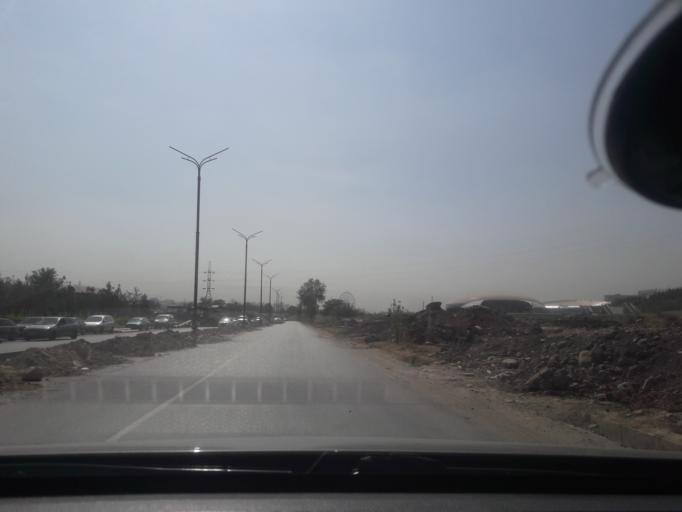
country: TJ
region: Dushanbe
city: Dushanbe
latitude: 38.6070
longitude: 68.7719
